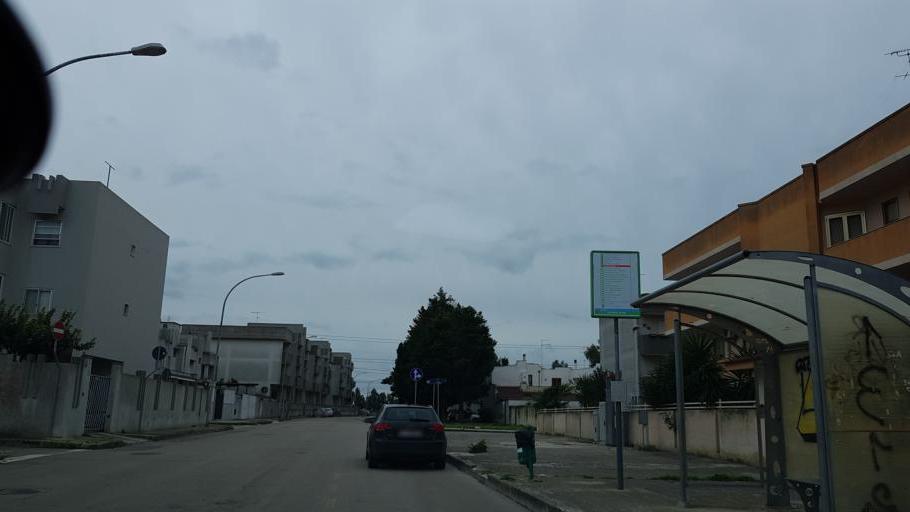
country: IT
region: Apulia
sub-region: Provincia di Brindisi
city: La Rosa
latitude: 40.6050
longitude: 17.9517
